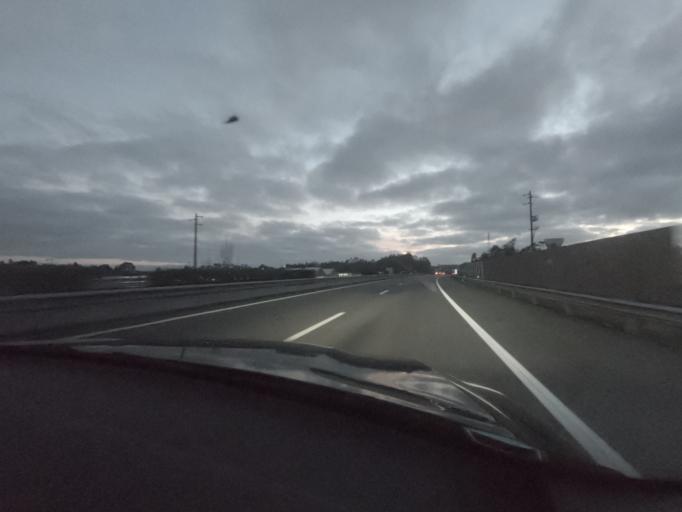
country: PT
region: Leiria
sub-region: Pombal
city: Pombal
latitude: 39.9460
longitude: -8.6724
